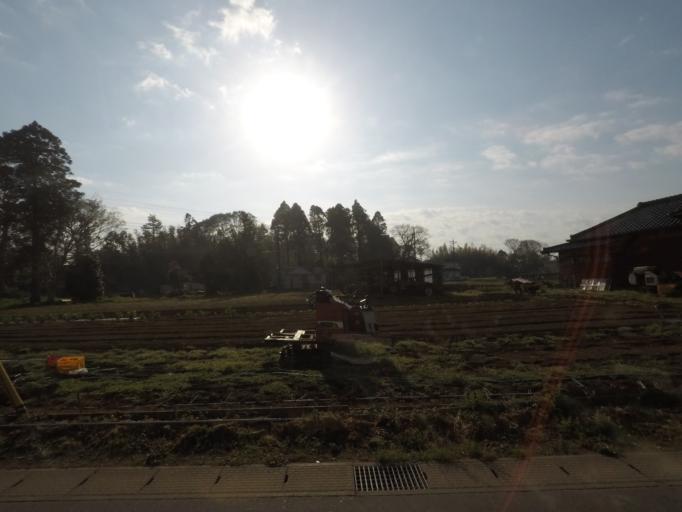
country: JP
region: Chiba
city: Yachimata
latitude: 35.6411
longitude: 140.2881
